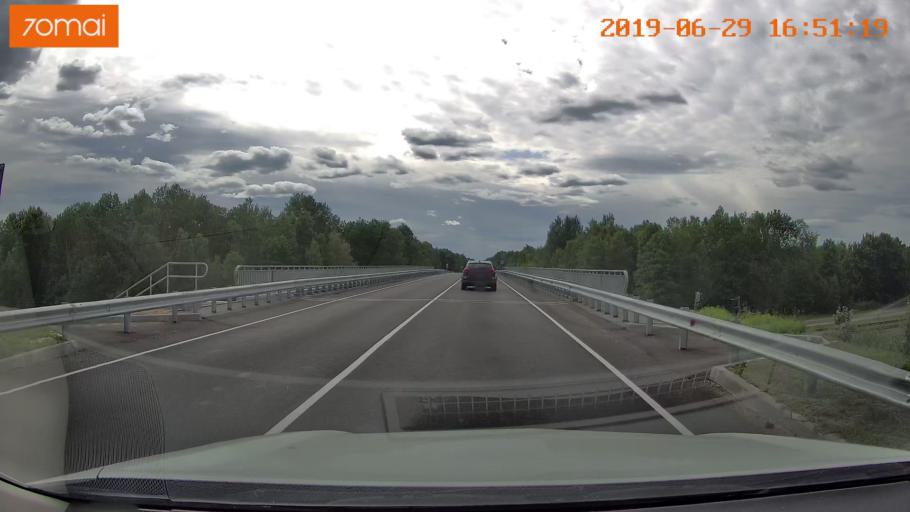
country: BY
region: Brest
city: Luninyets
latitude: 52.2806
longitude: 26.8267
